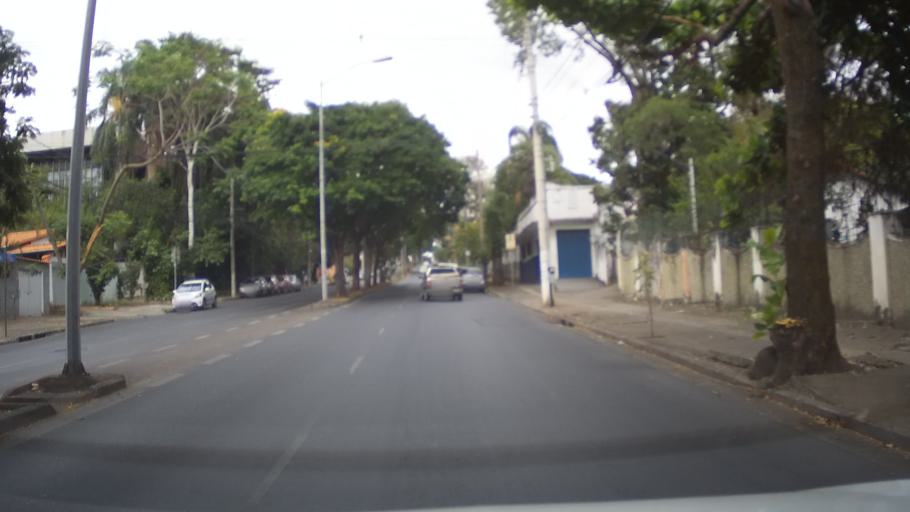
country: BR
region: Minas Gerais
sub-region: Belo Horizonte
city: Belo Horizonte
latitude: -19.8511
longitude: -43.9580
